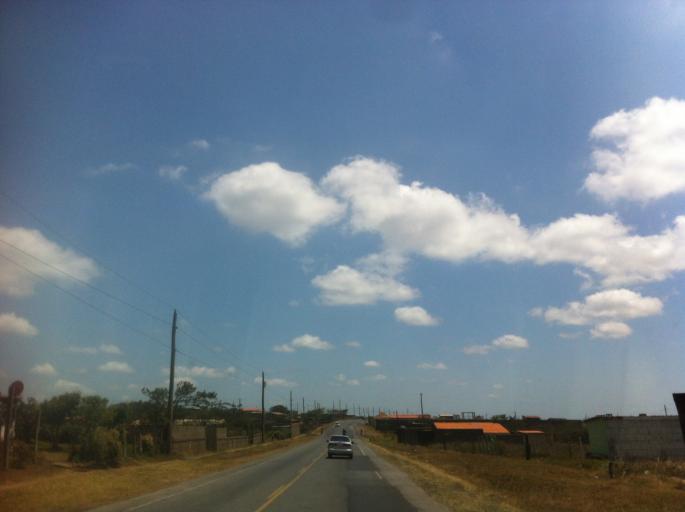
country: NI
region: Managua
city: El Crucero
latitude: 11.9603
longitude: -86.3043
